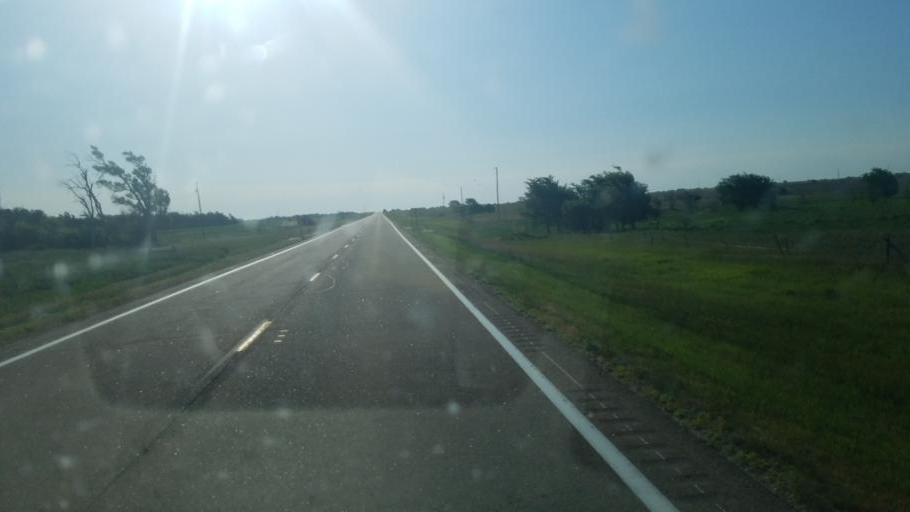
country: US
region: Kansas
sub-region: Edwards County
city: Kinsley
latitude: 38.1897
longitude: -99.4867
